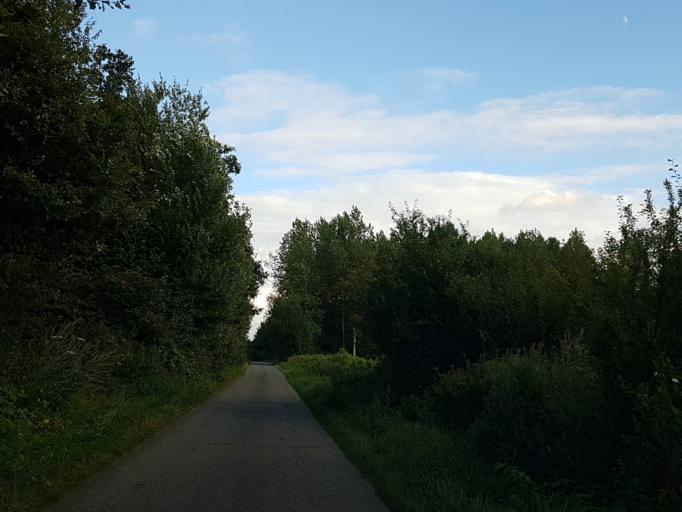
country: BE
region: Flanders
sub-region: Provincie Vlaams-Brabant
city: Bertem
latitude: 50.9151
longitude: 4.6081
